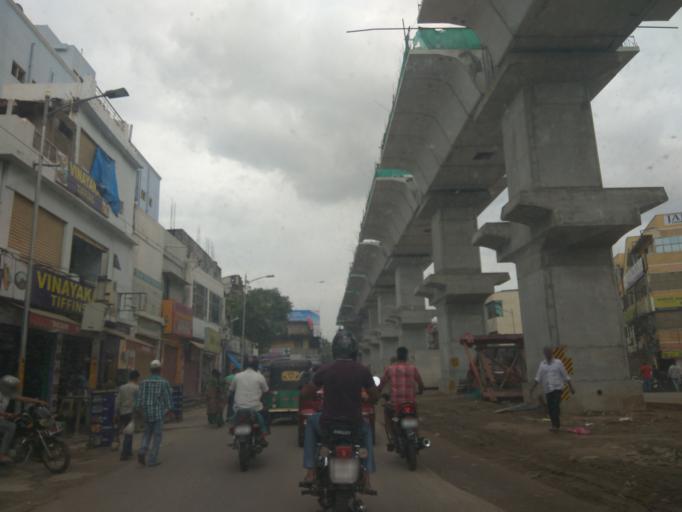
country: IN
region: Telangana
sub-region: Hyderabad
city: Hyderabad
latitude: 17.4014
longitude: 78.4950
